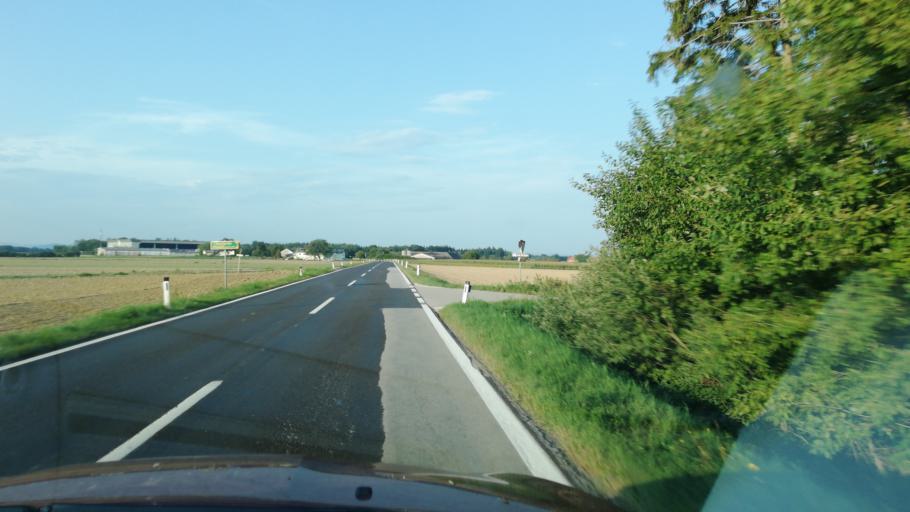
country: AT
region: Upper Austria
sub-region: Politischer Bezirk Steyr-Land
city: Sierning
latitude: 48.1169
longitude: 14.3322
